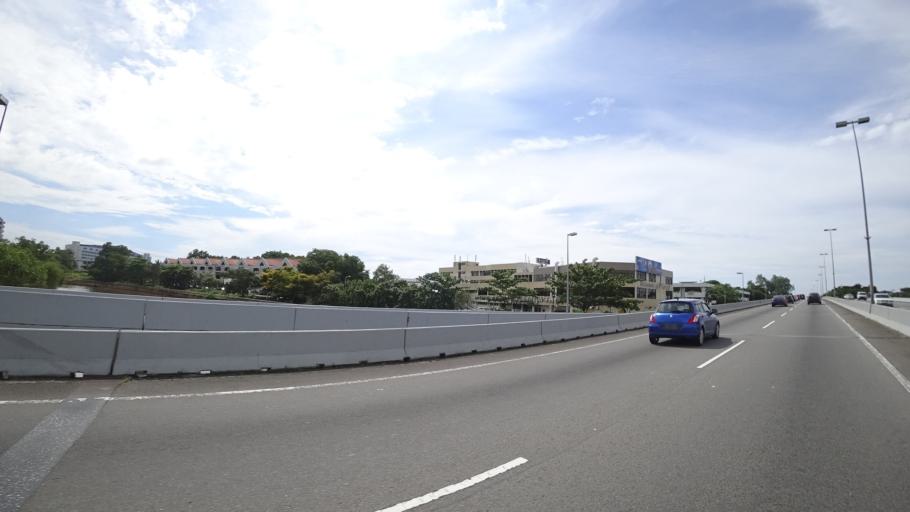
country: BN
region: Brunei and Muara
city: Bandar Seri Begawan
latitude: 4.9073
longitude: 114.9205
